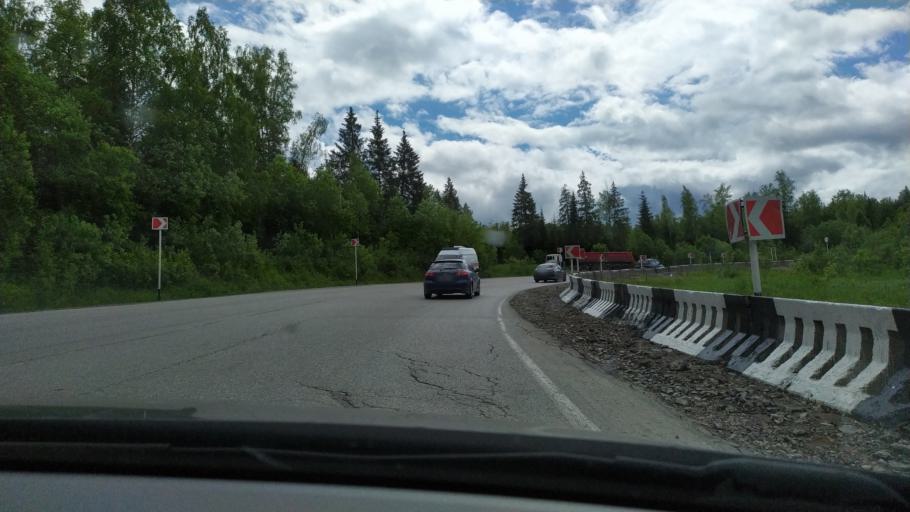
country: RU
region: Perm
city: Gremyachinsk
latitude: 58.4410
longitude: 57.8873
